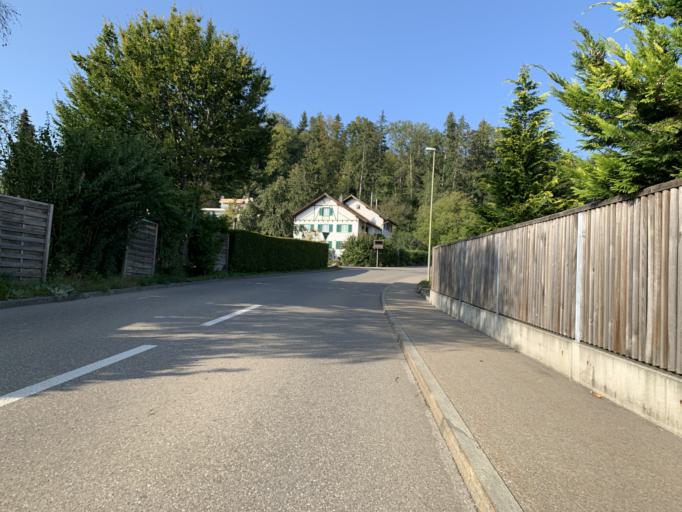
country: CH
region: Zurich
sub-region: Bezirk Hinwil
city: Hinwil
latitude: 47.3058
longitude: 8.8483
